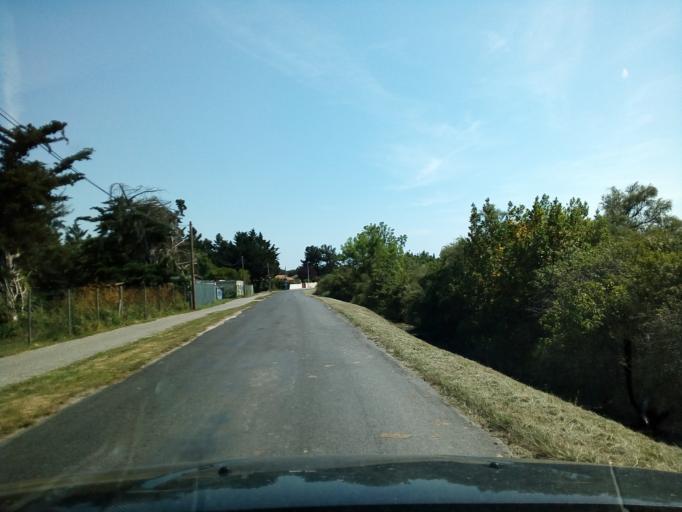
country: FR
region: Poitou-Charentes
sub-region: Departement de la Charente-Maritime
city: Boyard-Ville
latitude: 45.9764
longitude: -1.2984
